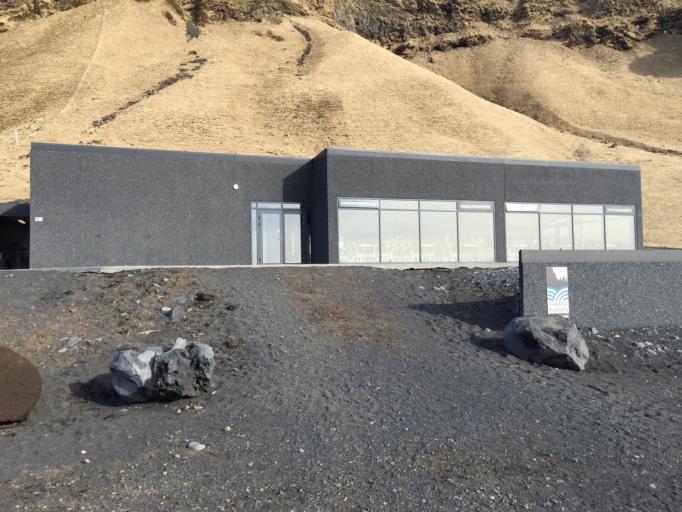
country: IS
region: South
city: Vestmannaeyjar
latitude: 63.4042
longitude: -19.0443
